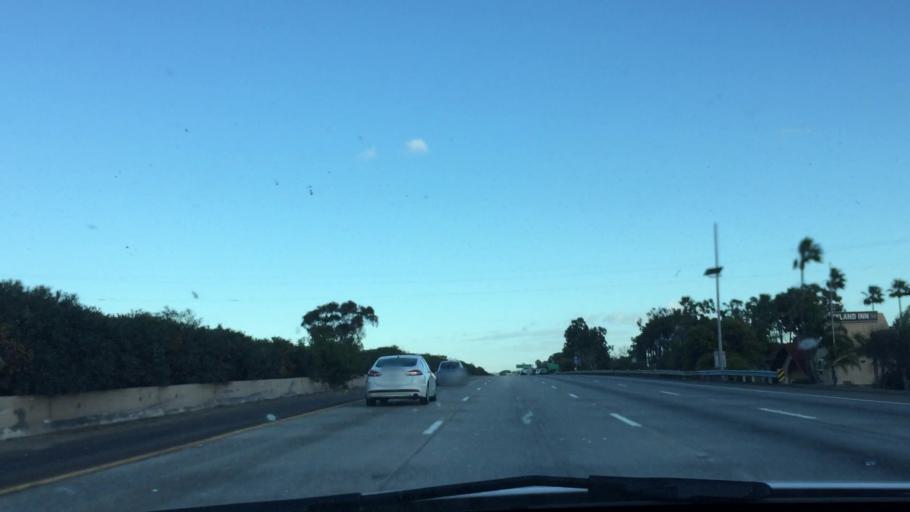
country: US
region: California
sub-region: San Diego County
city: Carlsbad
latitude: 33.1560
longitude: -117.3385
